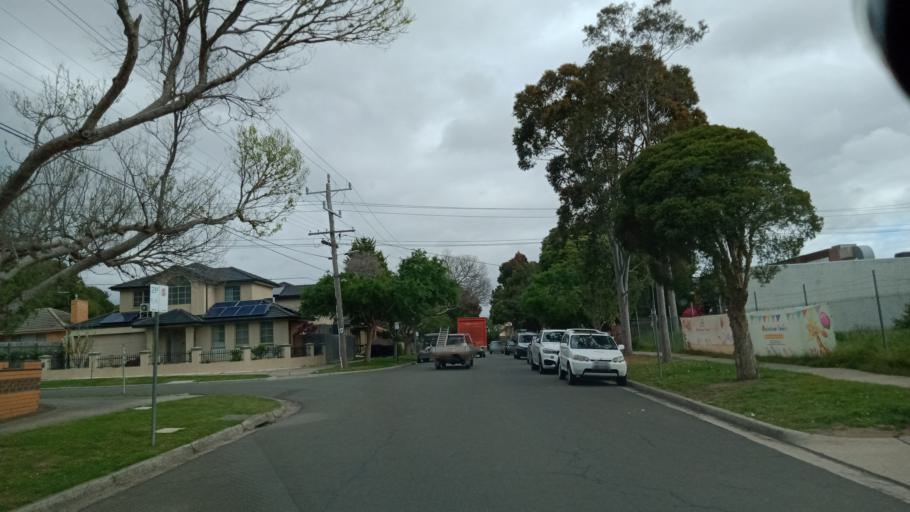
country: AU
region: Victoria
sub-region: Monash
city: Notting Hill
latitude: -37.8872
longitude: 145.1596
